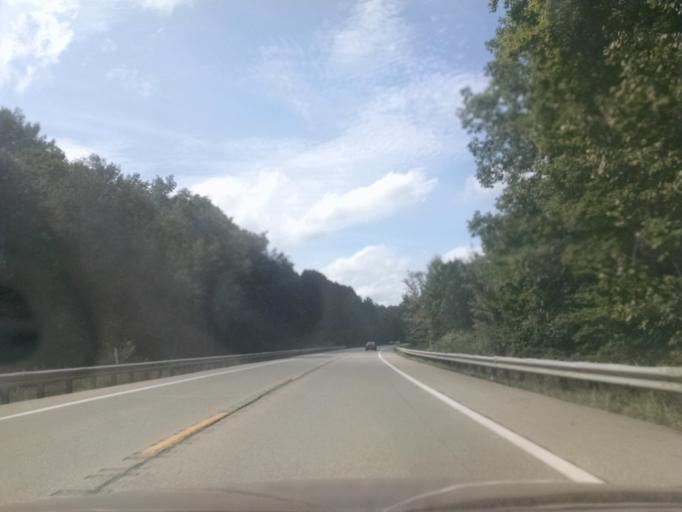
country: US
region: Michigan
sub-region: Clare County
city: Clare
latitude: 43.8707
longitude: -84.9333
